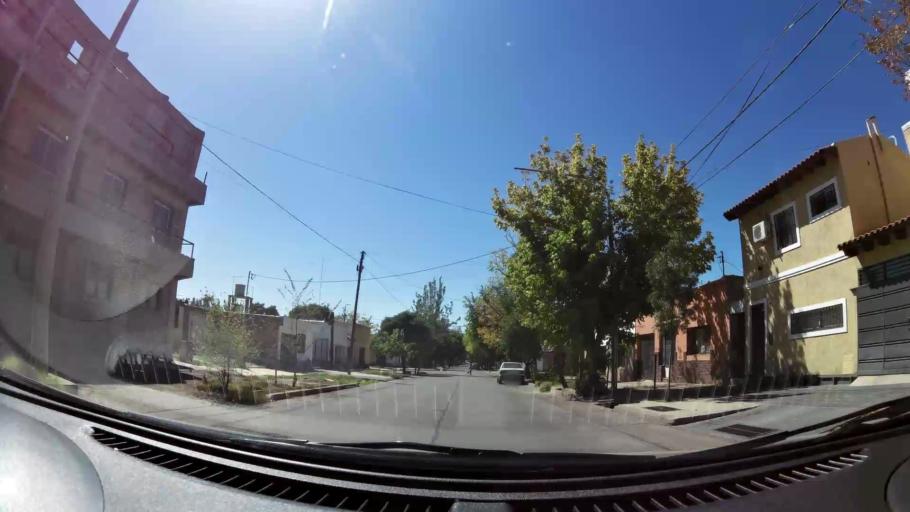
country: AR
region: Mendoza
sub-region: Departamento de Godoy Cruz
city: Godoy Cruz
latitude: -32.9047
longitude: -68.8627
